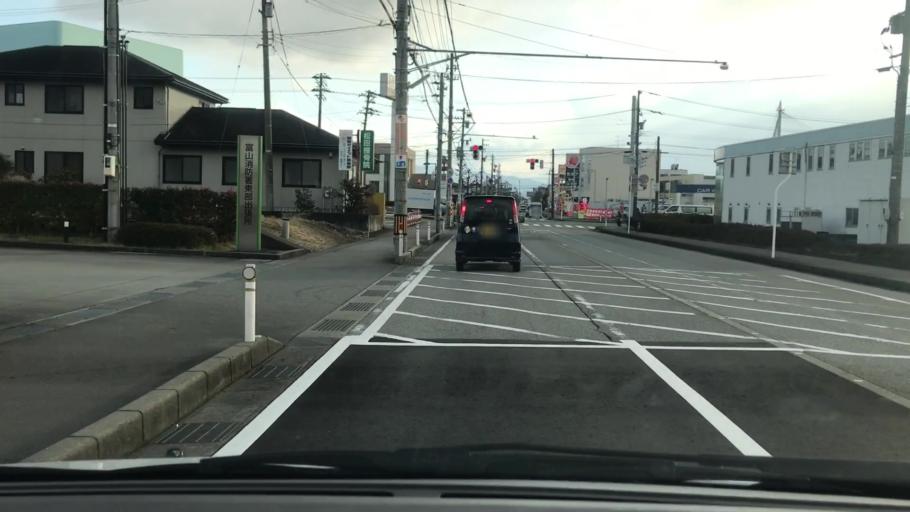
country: JP
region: Toyama
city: Toyama-shi
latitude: 36.6782
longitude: 137.2369
